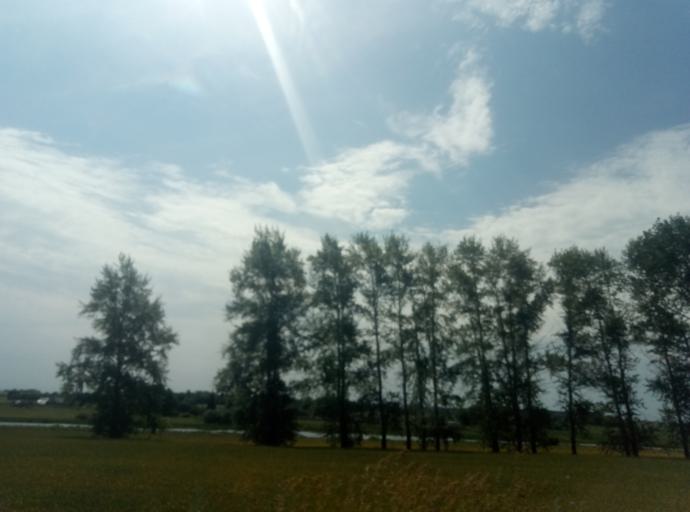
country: RU
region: Tula
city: Kireyevsk
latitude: 53.8976
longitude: 37.9939
